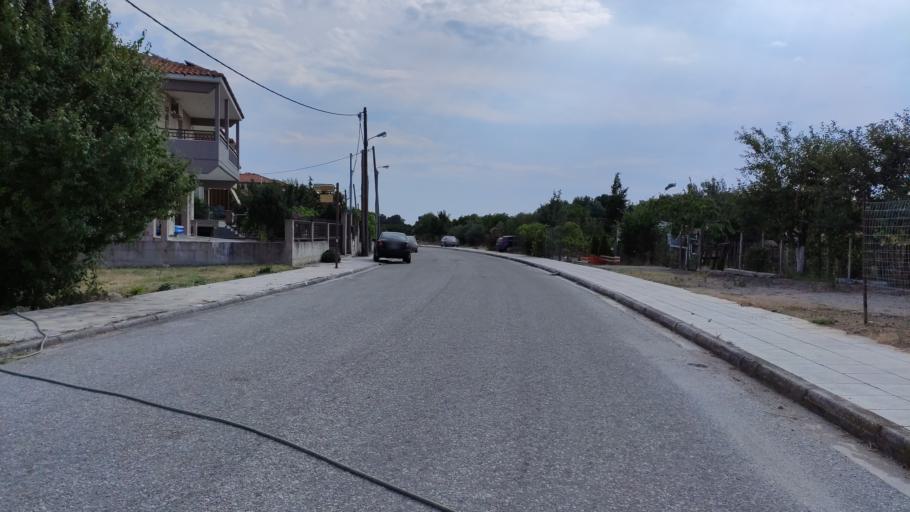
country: GR
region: East Macedonia and Thrace
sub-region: Nomos Rodopis
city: Komotini
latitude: 41.1324
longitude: 25.3917
